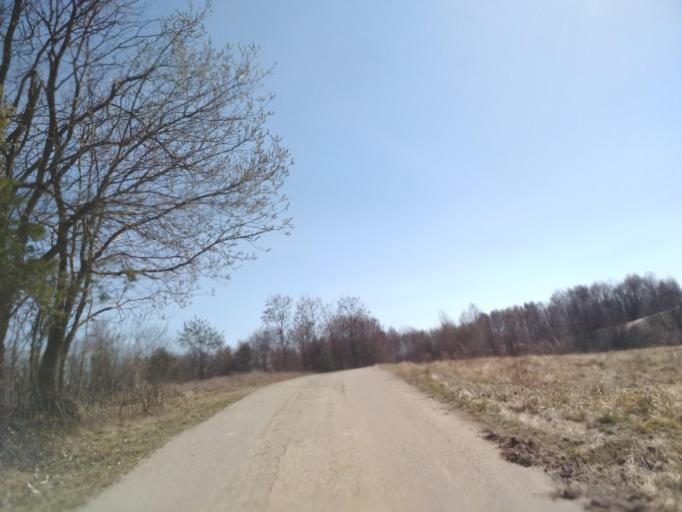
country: PL
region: Subcarpathian Voivodeship
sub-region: Powiat brzozowski
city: Jablonica Polska
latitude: 49.7464
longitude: 21.8923
